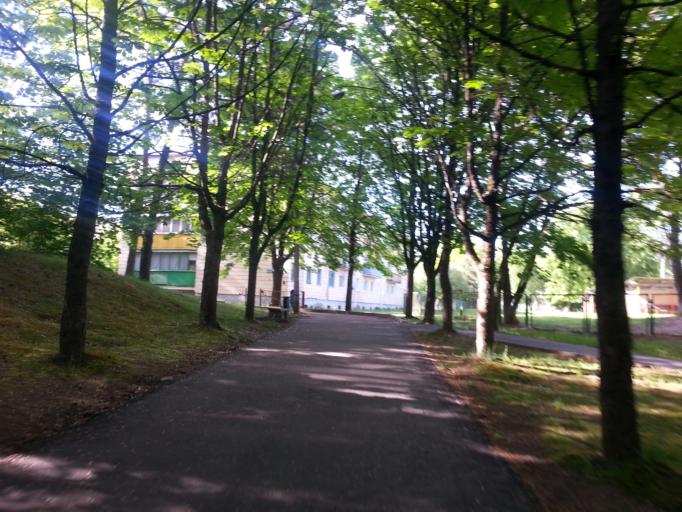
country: BY
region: Minsk
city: Narach
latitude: 54.9097
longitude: 26.7060
